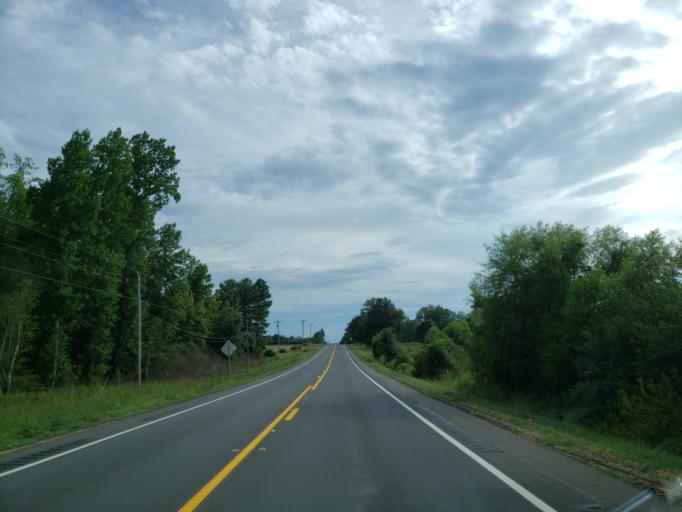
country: US
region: Georgia
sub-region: Irwin County
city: Ocilla
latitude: 31.5551
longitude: -83.3705
